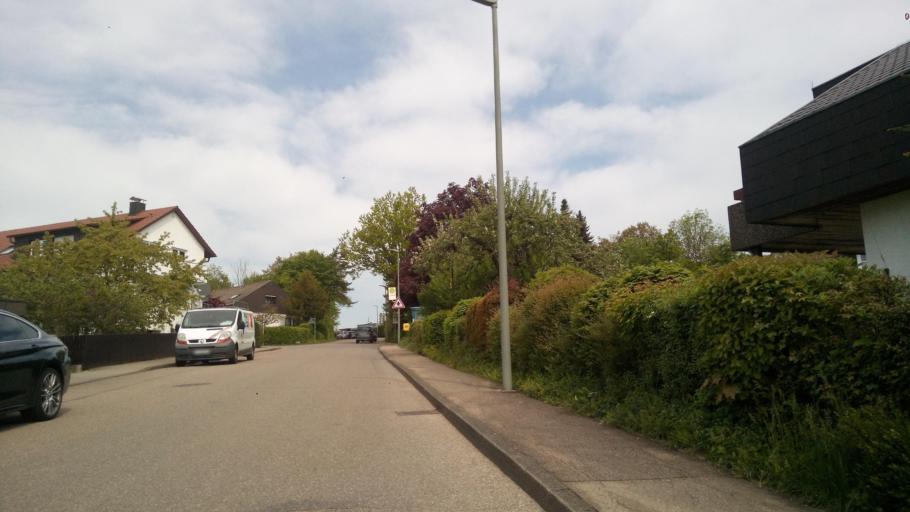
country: DE
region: Baden-Wuerttemberg
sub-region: Regierungsbezirk Stuttgart
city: Eislingen
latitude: 48.7061
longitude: 9.7084
